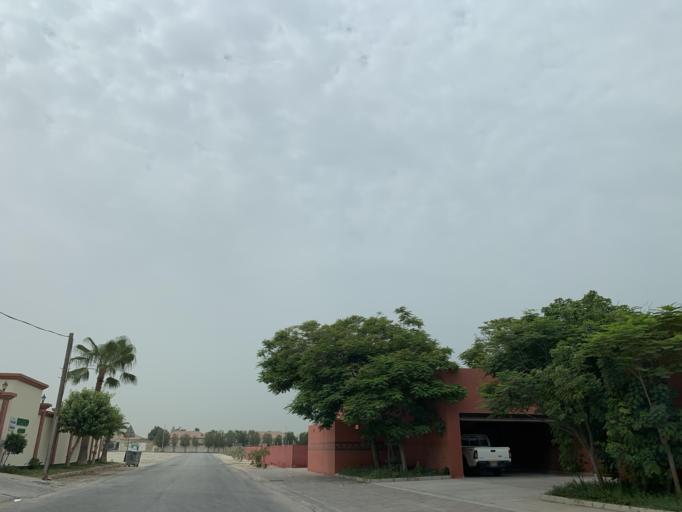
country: BH
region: Central Governorate
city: Madinat Hamad
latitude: 26.1809
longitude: 50.4712
